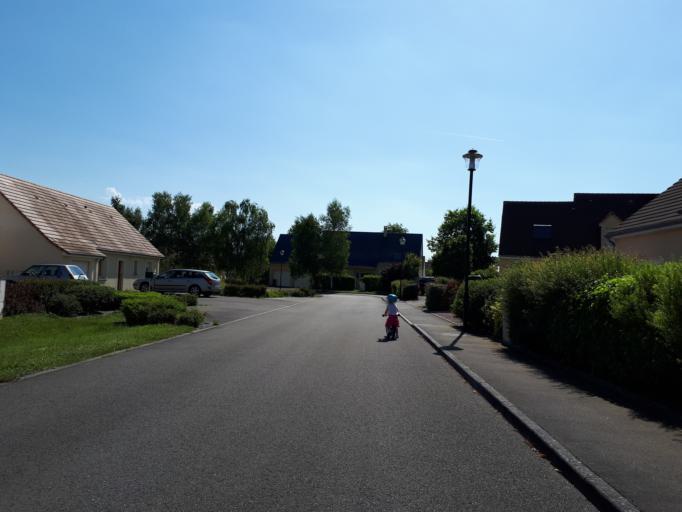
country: FR
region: Pays de la Loire
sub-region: Departement de la Sarthe
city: Champagne
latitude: 48.0776
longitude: 0.2884
